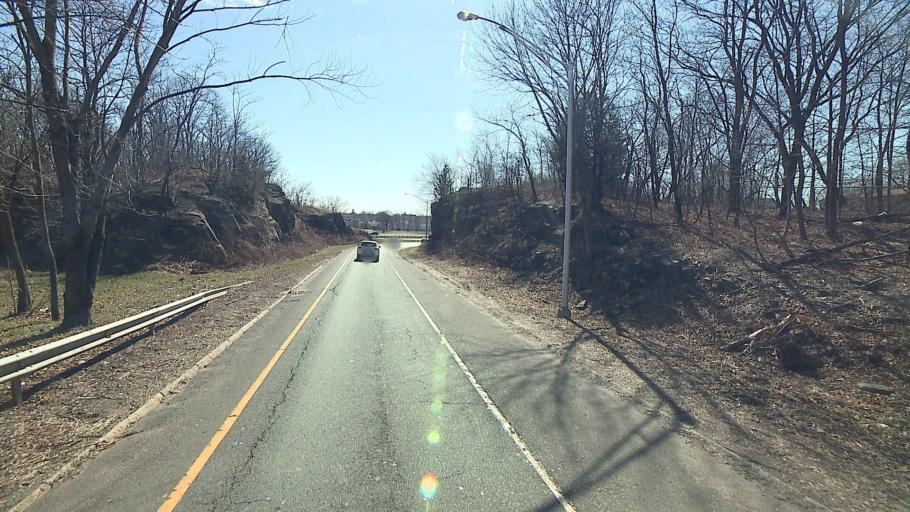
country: US
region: Connecticut
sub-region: Fairfield County
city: Trumbull
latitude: 41.2055
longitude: -73.1930
